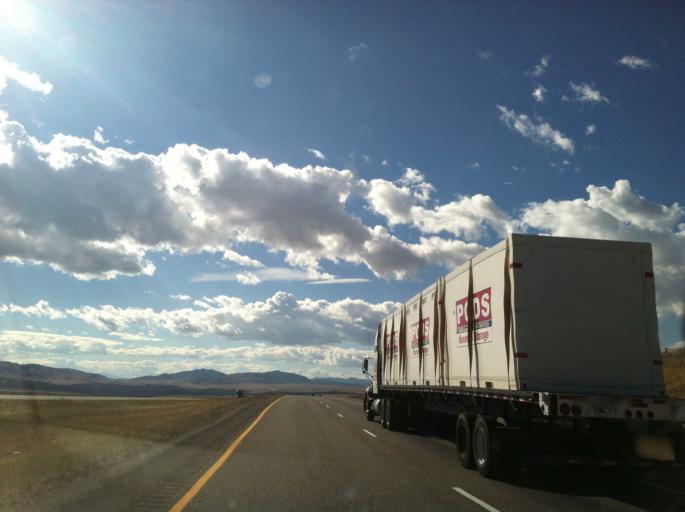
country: US
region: Montana
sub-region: Gallatin County
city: Three Forks
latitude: 45.9194
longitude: -111.6708
